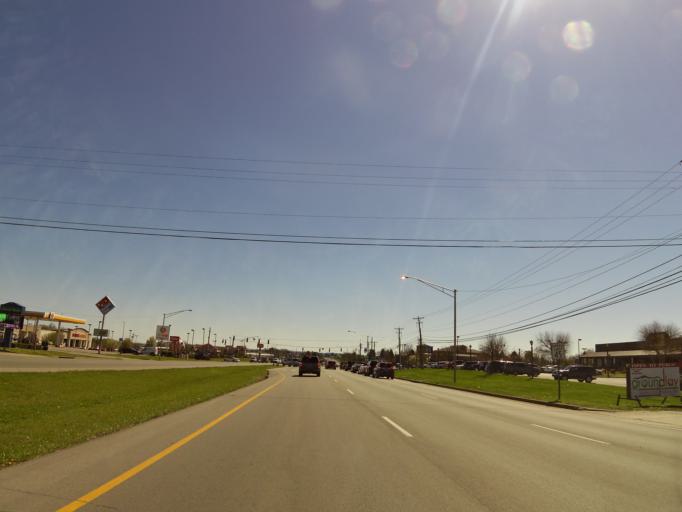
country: US
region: Kentucky
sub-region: Pulaski County
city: Somerset
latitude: 37.0683
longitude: -84.6197
